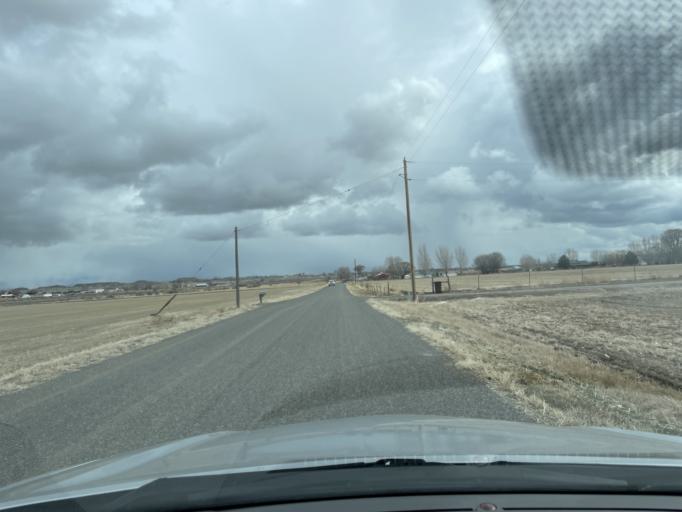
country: US
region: Colorado
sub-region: Mesa County
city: Loma
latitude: 39.1860
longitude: -108.8075
